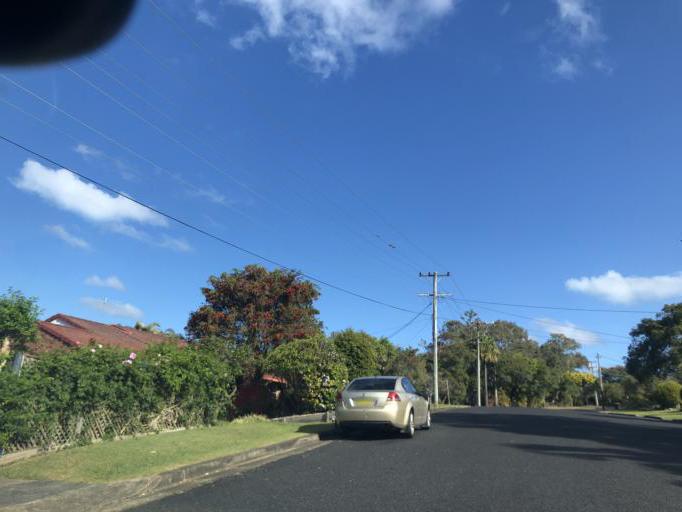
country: AU
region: New South Wales
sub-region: Coffs Harbour
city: Woolgoolga
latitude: -30.0947
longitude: 153.1971
